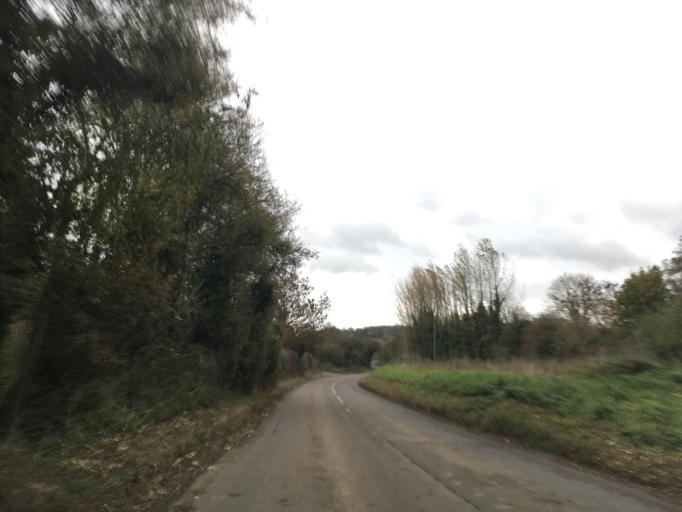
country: GB
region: England
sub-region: South Gloucestershire
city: Hinton
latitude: 51.4888
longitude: -2.3954
